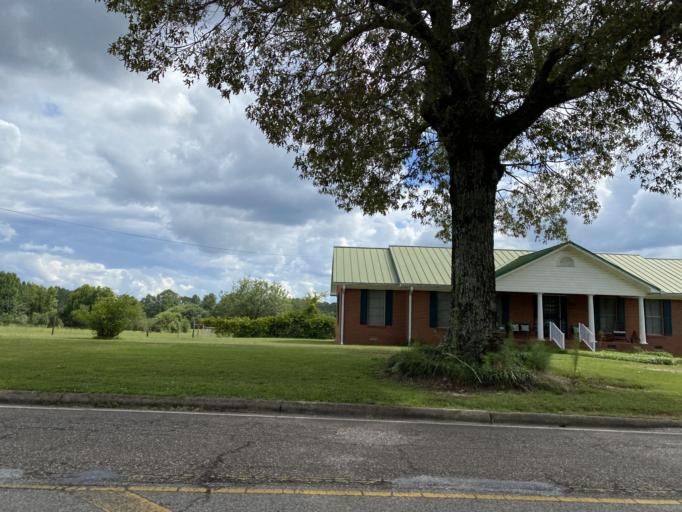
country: US
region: Mississippi
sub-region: Monroe County
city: Amory
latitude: 33.9769
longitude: -88.4195
